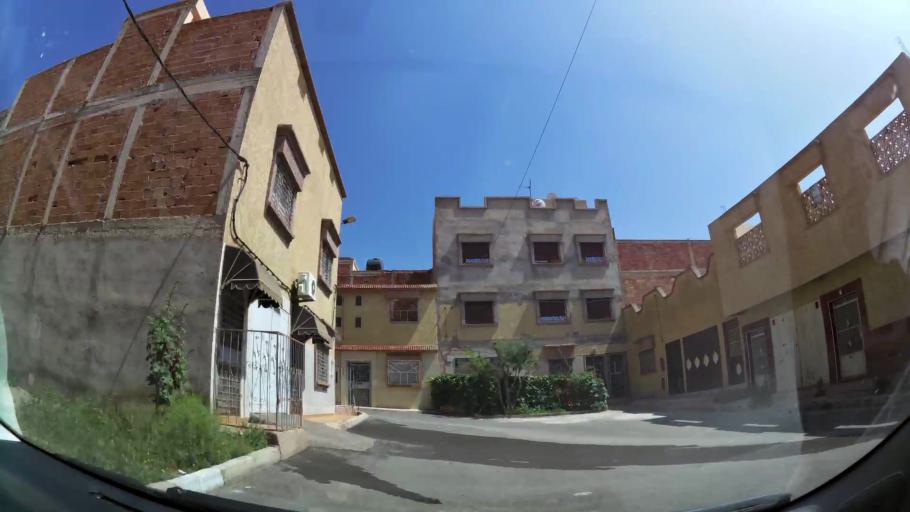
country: MA
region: Oriental
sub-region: Oujda-Angad
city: Oujda
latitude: 34.6903
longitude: -1.8823
